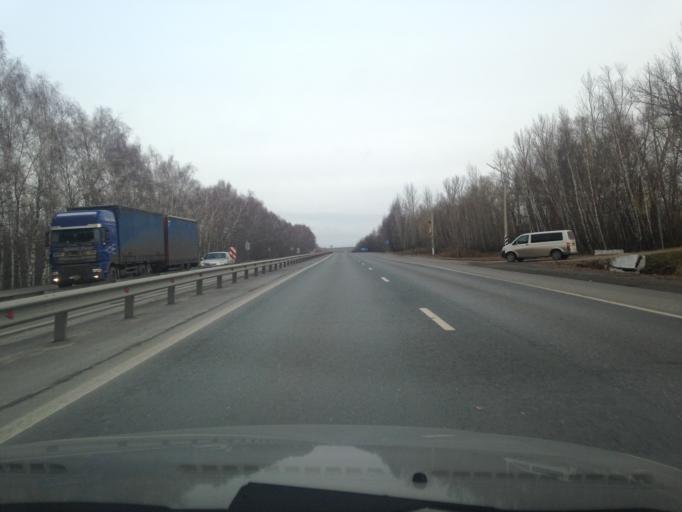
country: RU
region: Ulyanovsk
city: Novoul'yanovsk
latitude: 54.1958
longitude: 48.2838
